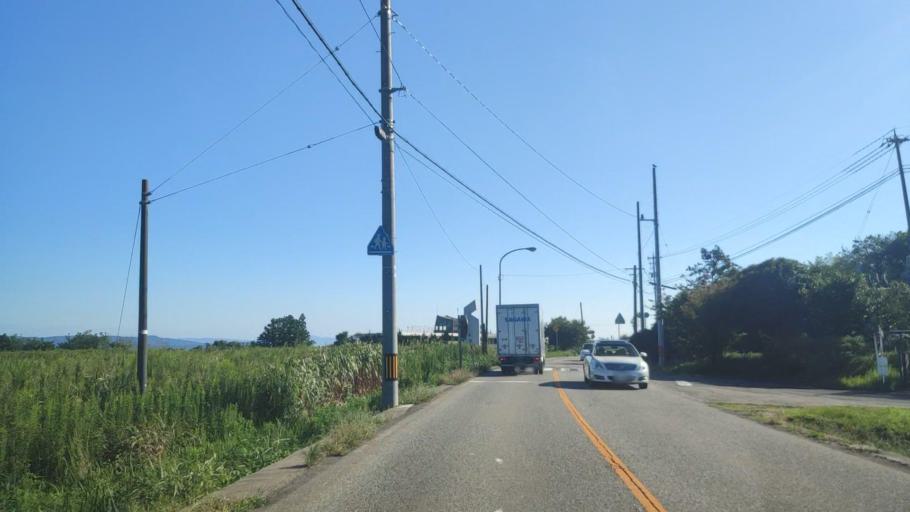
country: JP
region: Ishikawa
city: Nanao
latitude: 37.1945
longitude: 136.9109
